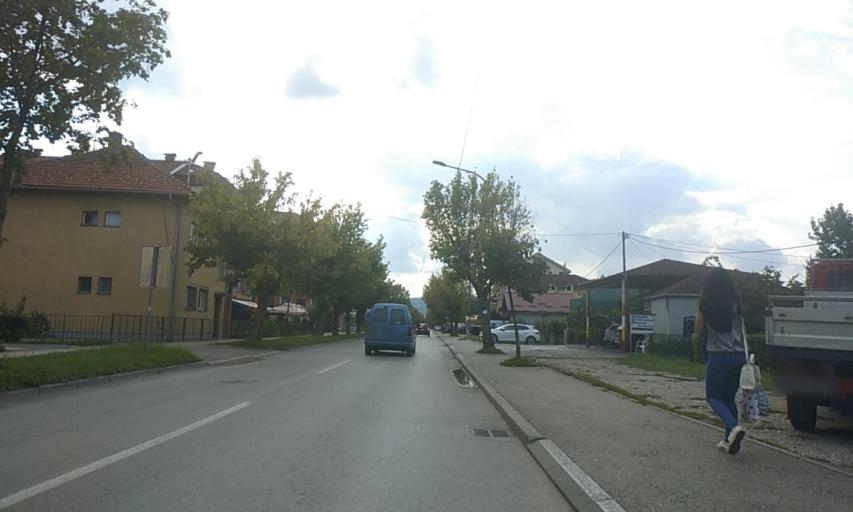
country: BA
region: Republika Srpska
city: Starcevica
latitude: 44.7653
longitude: 17.2032
